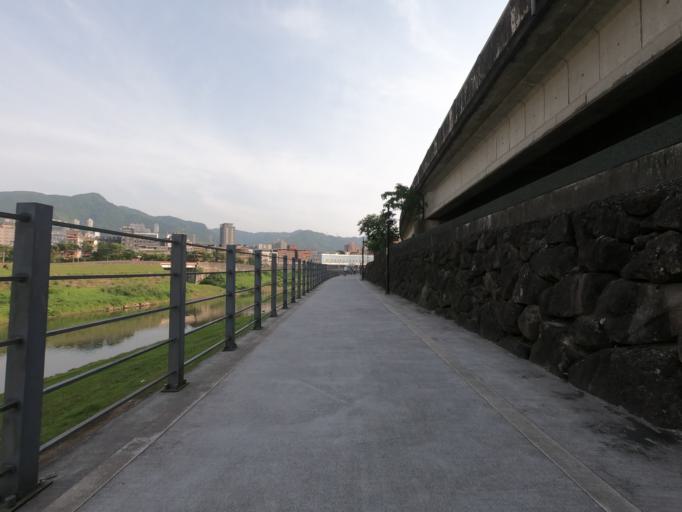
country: TW
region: Taiwan
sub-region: Keelung
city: Keelung
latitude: 25.0719
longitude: 121.6588
